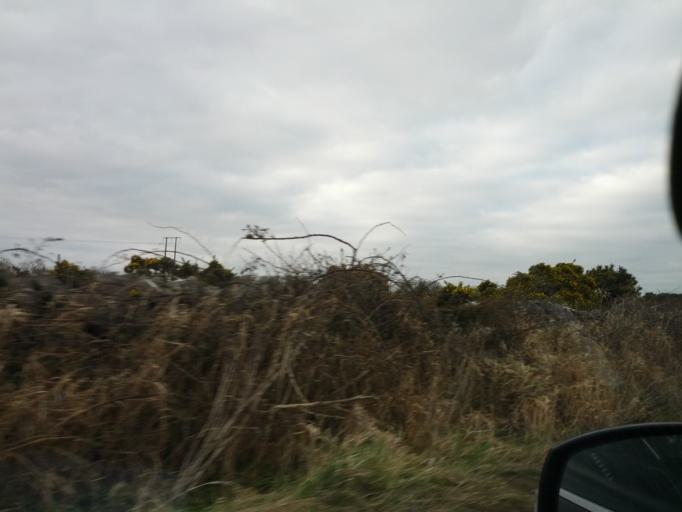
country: IE
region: Connaught
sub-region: County Galway
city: Gort
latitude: 53.1622
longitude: -8.8508
